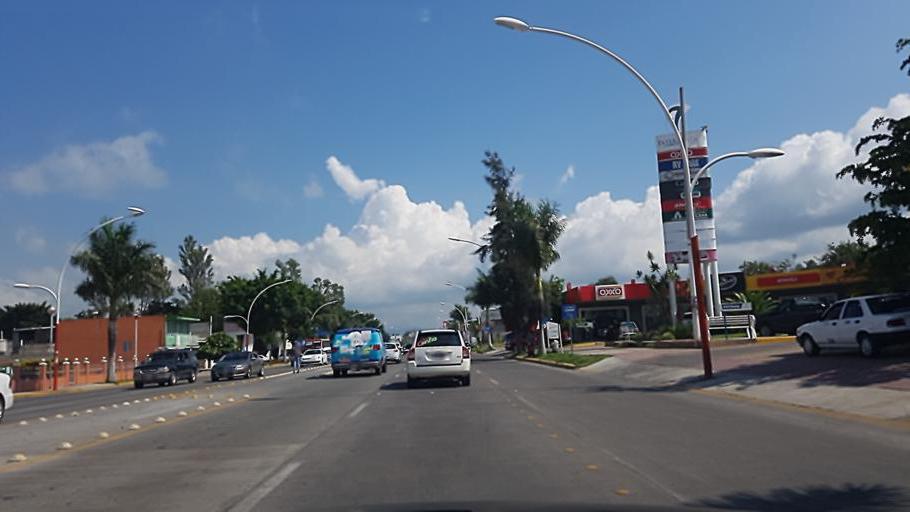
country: MX
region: Nayarit
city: Tepic
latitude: 21.4820
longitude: -104.8926
